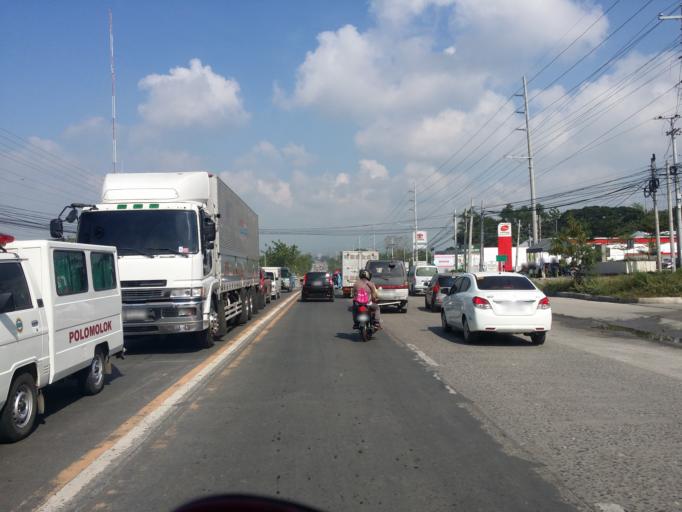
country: PH
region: Soccsksargen
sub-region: General Santos City
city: General Santos
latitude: 6.1187
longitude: 125.1612
